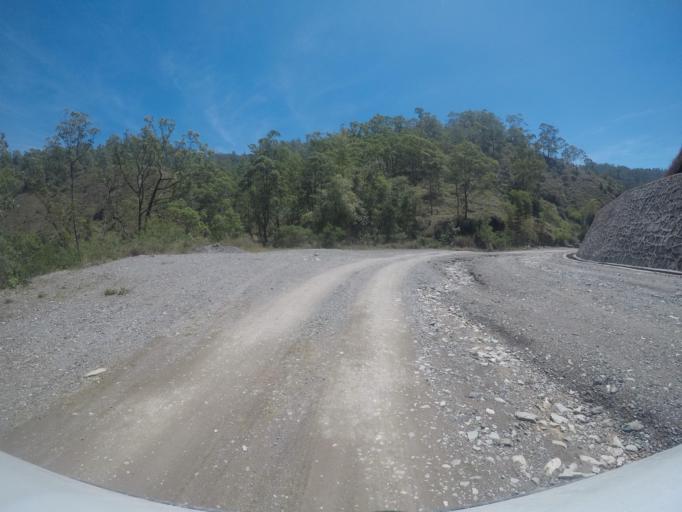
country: TL
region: Ermera
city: Gleno
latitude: -8.7793
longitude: 125.3818
